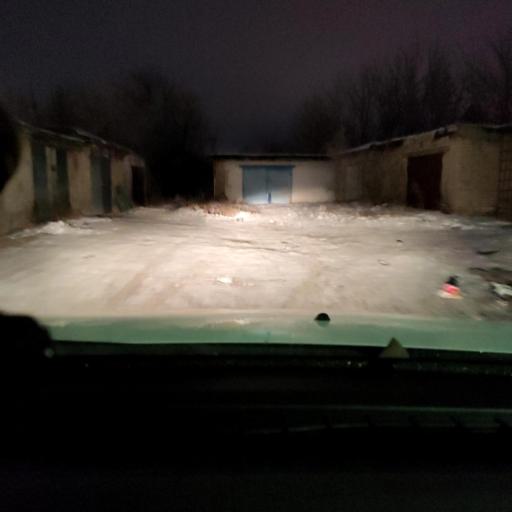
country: RU
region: Samara
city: Chapayevsk
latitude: 52.9902
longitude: 49.7171
